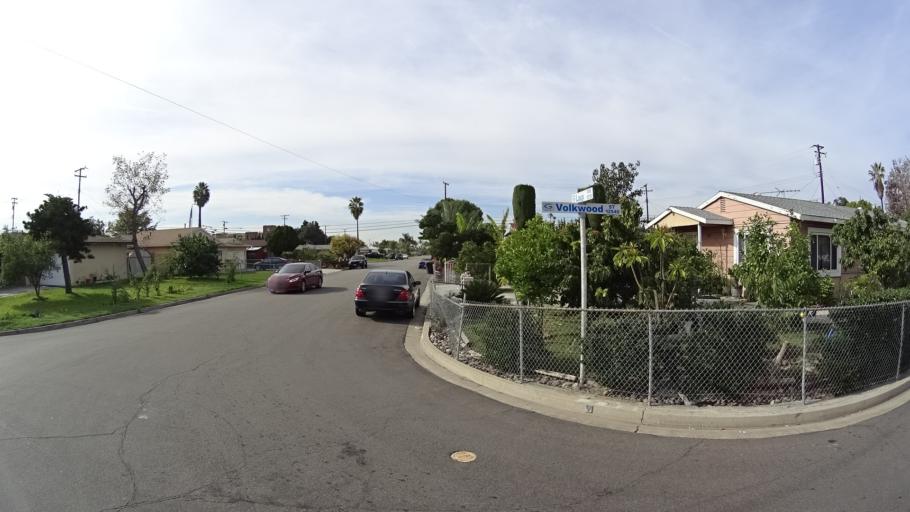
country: US
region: California
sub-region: Orange County
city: Garden Grove
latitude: 33.7810
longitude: -117.9110
